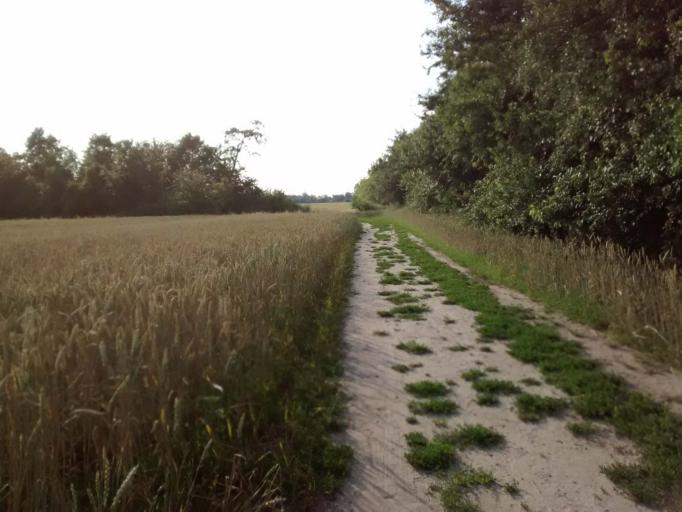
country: DE
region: Brandenburg
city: Hohen Neuendorf
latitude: 52.6541
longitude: 13.2756
